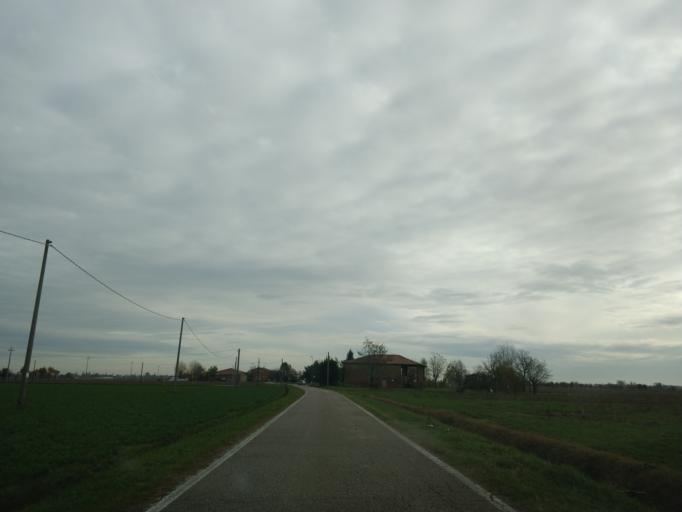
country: IT
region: Emilia-Romagna
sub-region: Provincia di Bologna
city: Argelato
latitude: 44.6363
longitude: 11.3204
